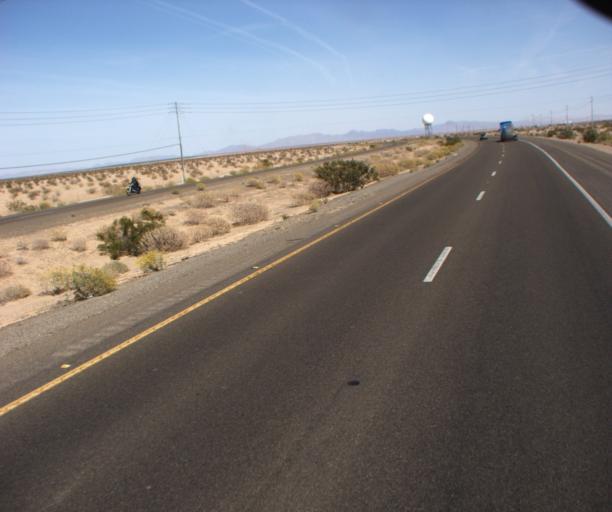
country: US
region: Arizona
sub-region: Yuma County
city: Somerton
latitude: 32.4945
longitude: -114.6638
